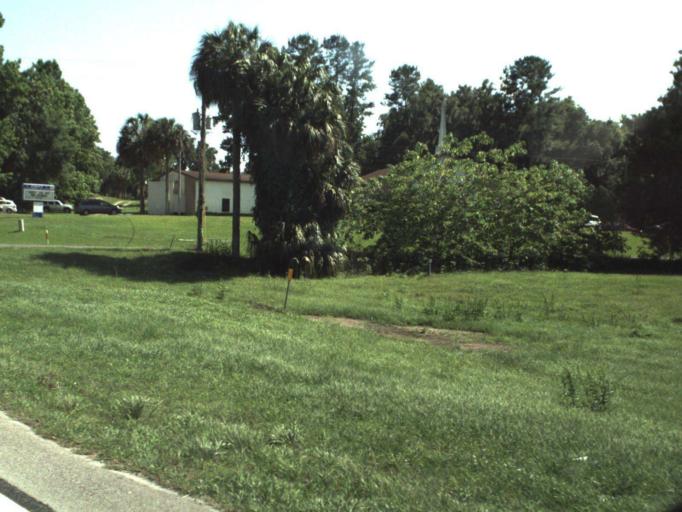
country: US
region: Florida
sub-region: Marion County
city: Belleview
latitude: 29.0776
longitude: -82.0752
